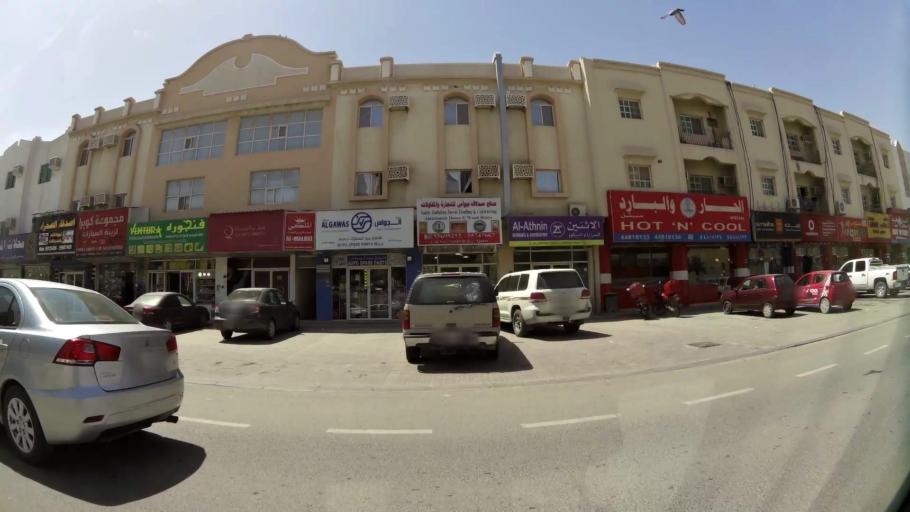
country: QA
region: Baladiyat ar Rayyan
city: Ar Rayyan
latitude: 25.2777
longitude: 51.4078
